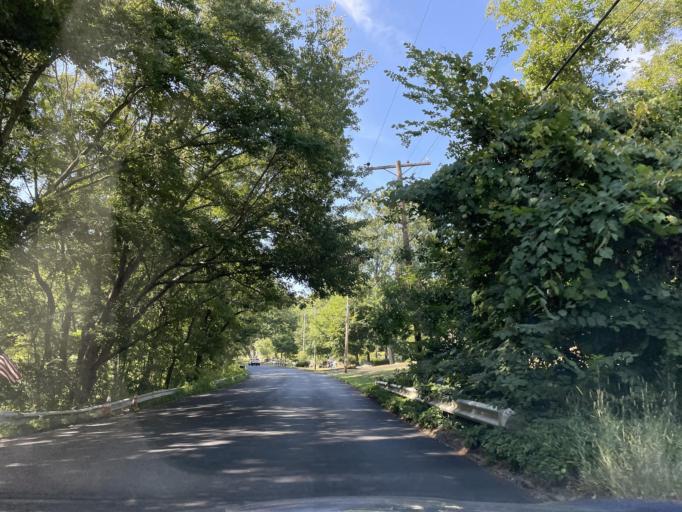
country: US
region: Massachusetts
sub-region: Worcester County
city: Northbridge
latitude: 42.1480
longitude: -71.6394
